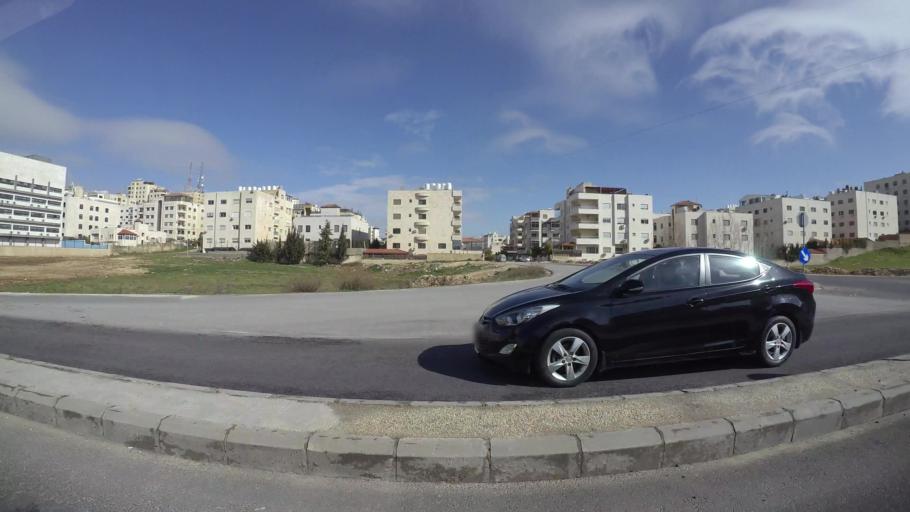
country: JO
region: Amman
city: Al Jubayhah
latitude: 32.0012
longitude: 35.8466
